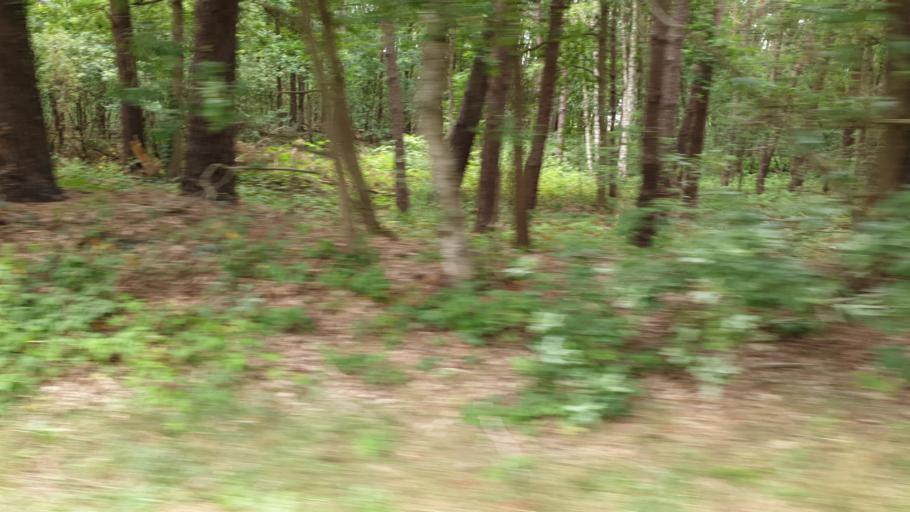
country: BE
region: Flanders
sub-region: Provincie Antwerpen
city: Meerhout
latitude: 51.1612
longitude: 5.0468
